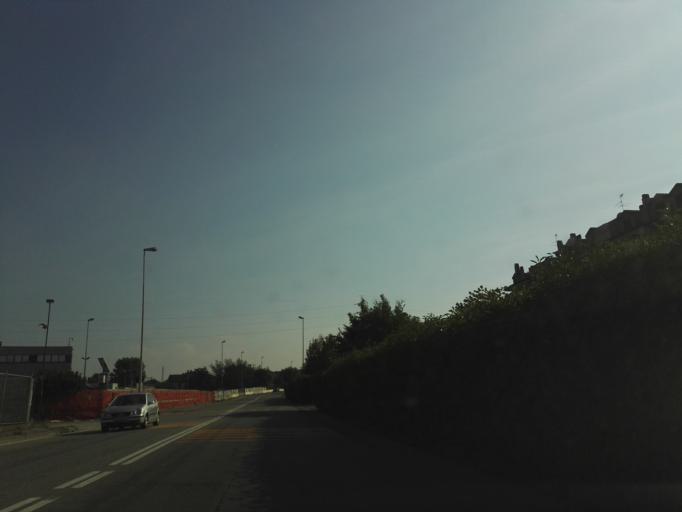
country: IT
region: Lombardy
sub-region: Citta metropolitana di Milano
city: Triginto
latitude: 45.3876
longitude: 9.3084
